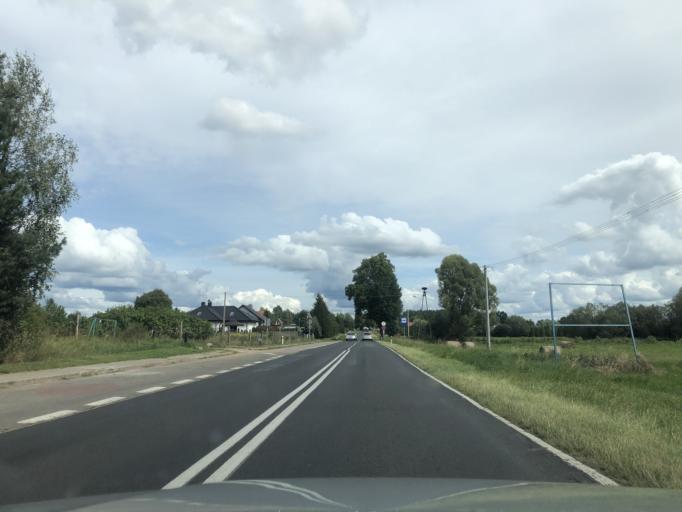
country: PL
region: Greater Poland Voivodeship
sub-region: Powiat pilski
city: Szydlowo
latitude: 53.0855
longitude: 16.6174
